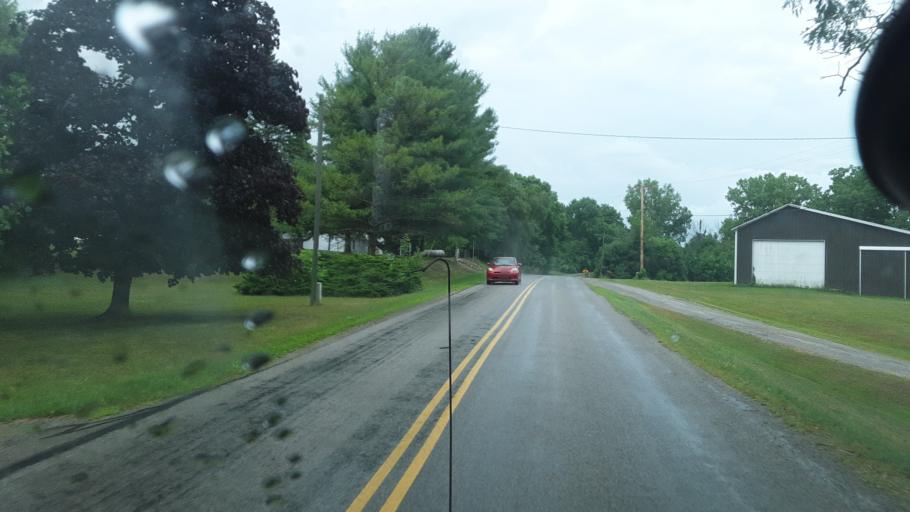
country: US
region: Indiana
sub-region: Steuben County
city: Hamilton
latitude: 41.6366
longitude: -84.7898
